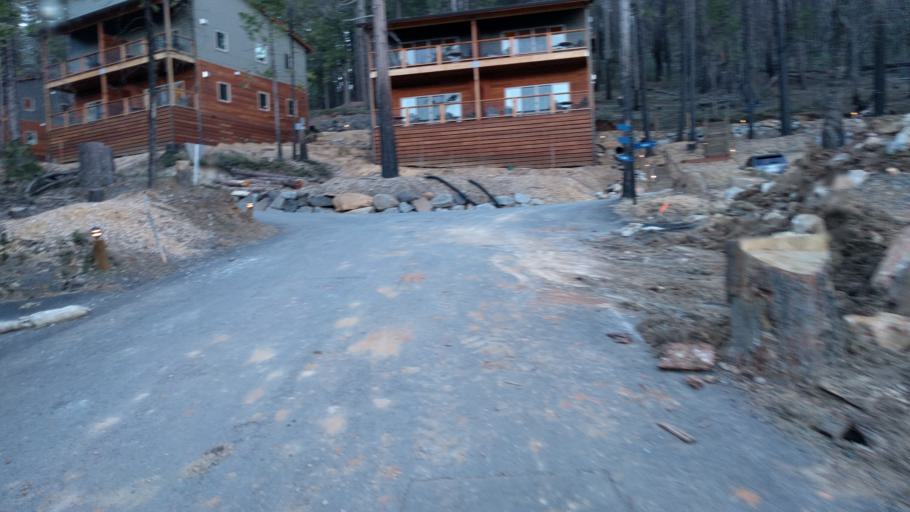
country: US
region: California
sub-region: Mariposa County
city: Midpines
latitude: 37.8126
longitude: -119.8803
